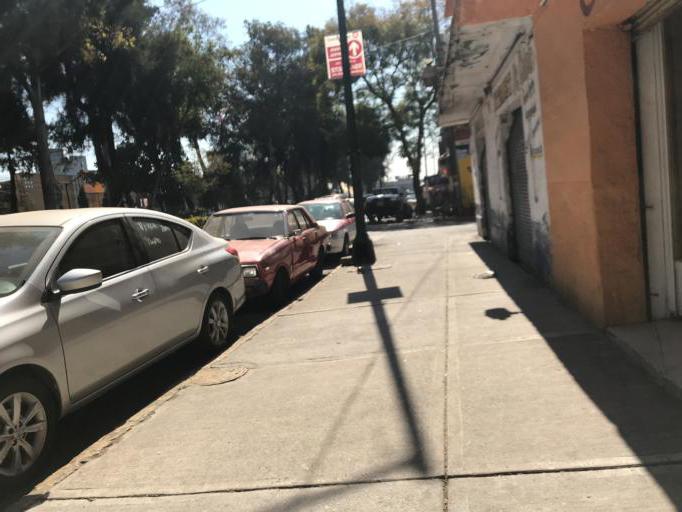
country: MX
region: Mexico City
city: Colonia Nativitas
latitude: 19.3995
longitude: -99.1245
